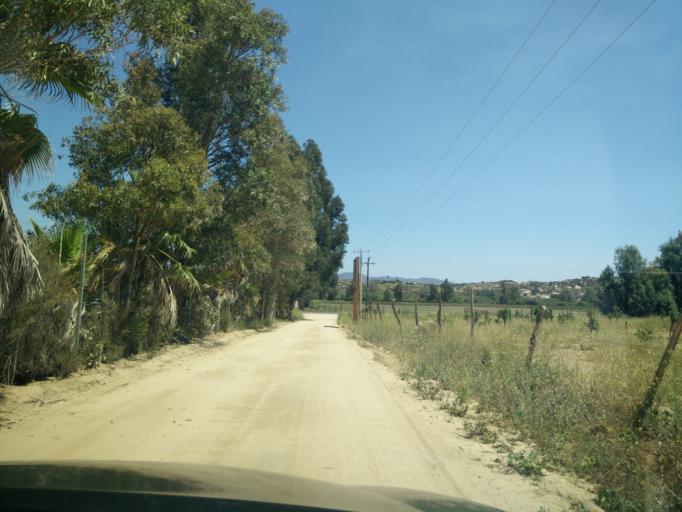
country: MX
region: Baja California
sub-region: Ensenada
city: Rancho Verde
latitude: 32.0494
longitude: -116.6638
